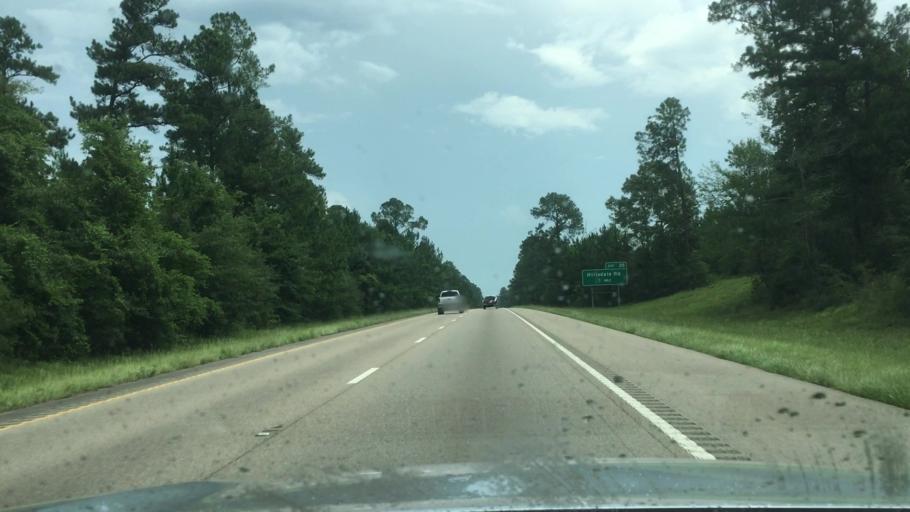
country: US
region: Mississippi
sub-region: Lamar County
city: Lumberton
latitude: 30.9080
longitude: -89.4679
